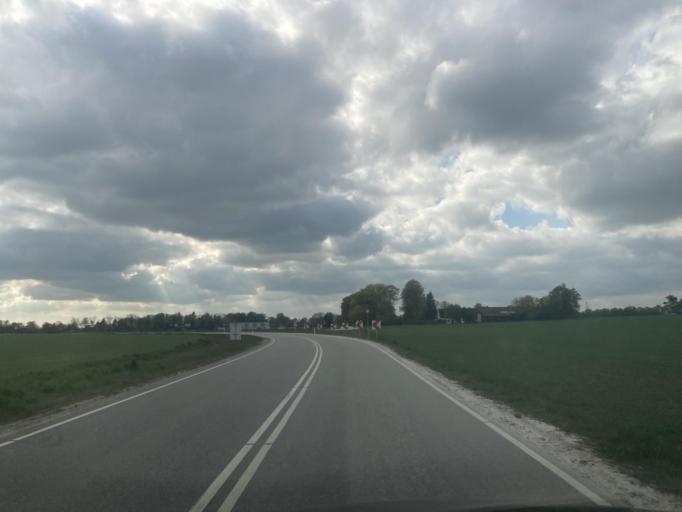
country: DK
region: Zealand
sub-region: Roskilde Kommune
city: Vindinge
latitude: 55.5985
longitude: 12.1219
